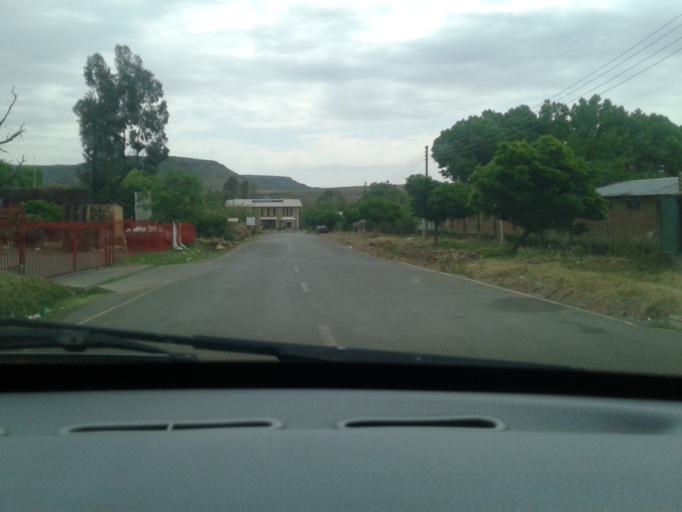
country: LS
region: Maseru
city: Maseru
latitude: -29.3002
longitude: 27.4720
